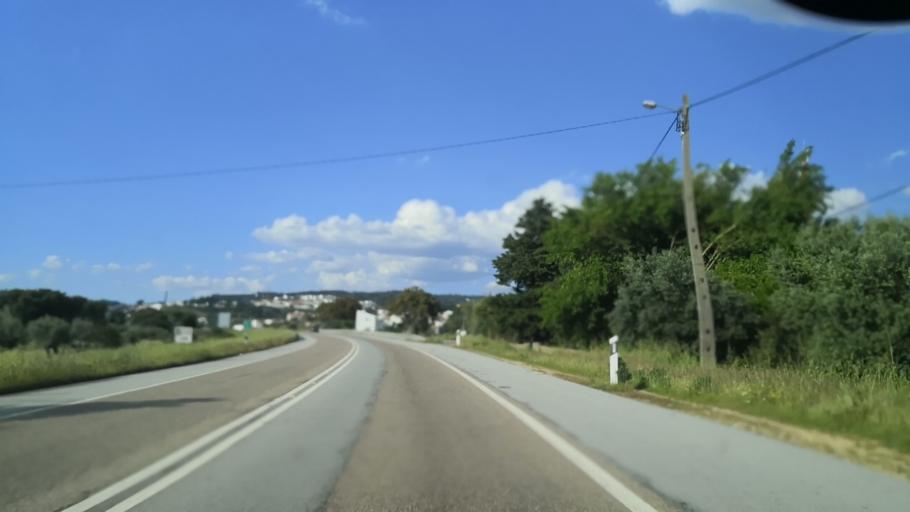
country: PT
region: Portalegre
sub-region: Portalegre
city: Portalegre
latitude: 39.2737
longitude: -7.4364
